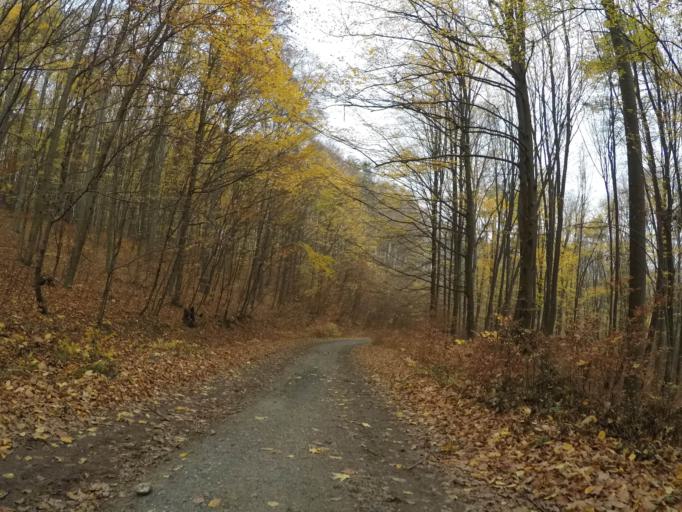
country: SK
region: Presovsky
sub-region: Okres Presov
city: Presov
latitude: 48.8868
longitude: 21.1985
